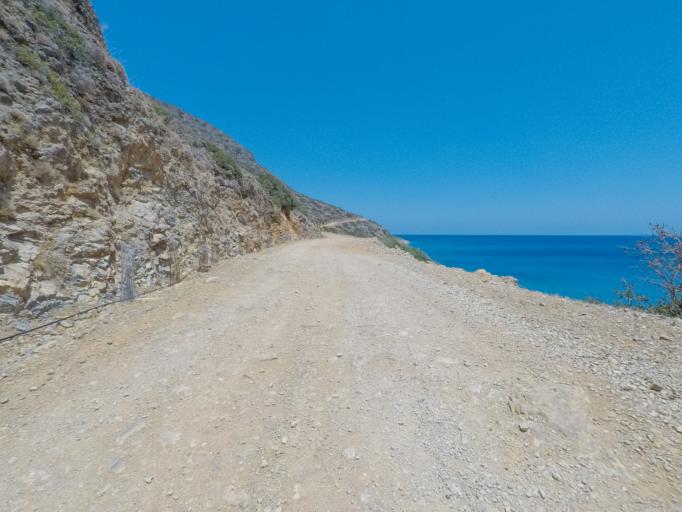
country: GR
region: Crete
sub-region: Nomos Lasithiou
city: Elounda
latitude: 35.3065
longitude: 25.7346
